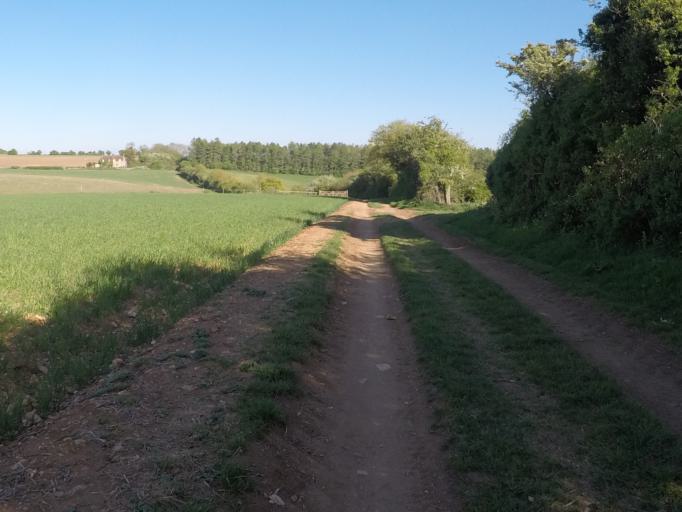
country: GB
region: England
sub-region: Oxfordshire
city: Stonesfield
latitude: 51.8574
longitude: -1.4505
